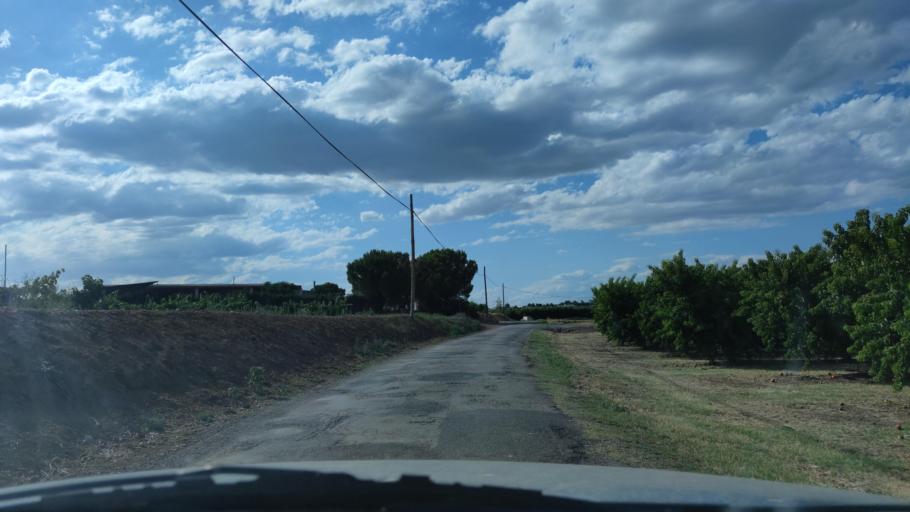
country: ES
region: Catalonia
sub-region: Provincia de Lleida
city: Alcarras
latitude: 41.5937
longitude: 0.5312
